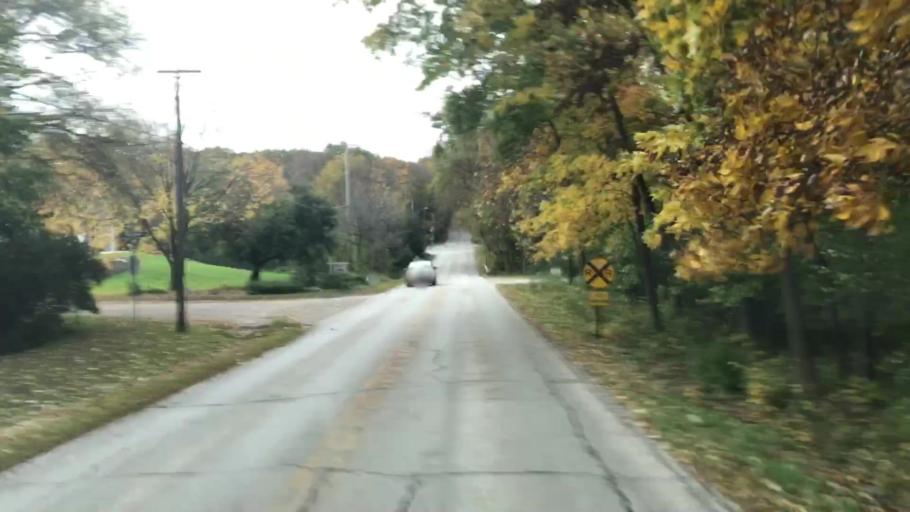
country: US
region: Wisconsin
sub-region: Waukesha County
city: Brookfield
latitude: 43.0570
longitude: -88.0964
